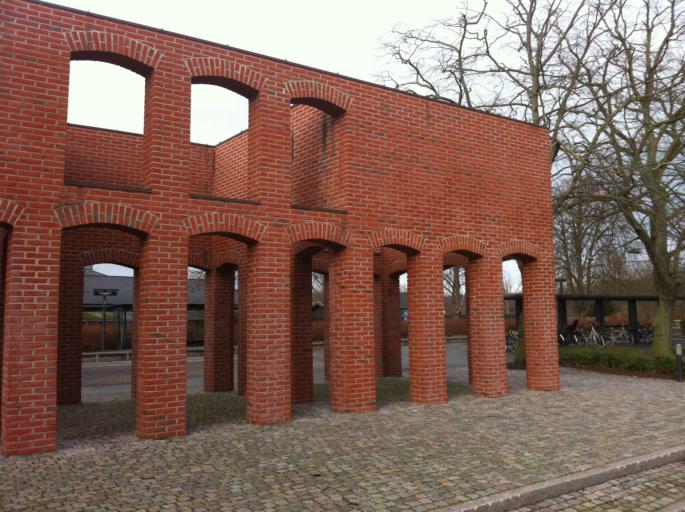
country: DK
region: Capital Region
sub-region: Fredensborg Kommune
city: Humlebaek
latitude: 55.9640
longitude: 12.5337
